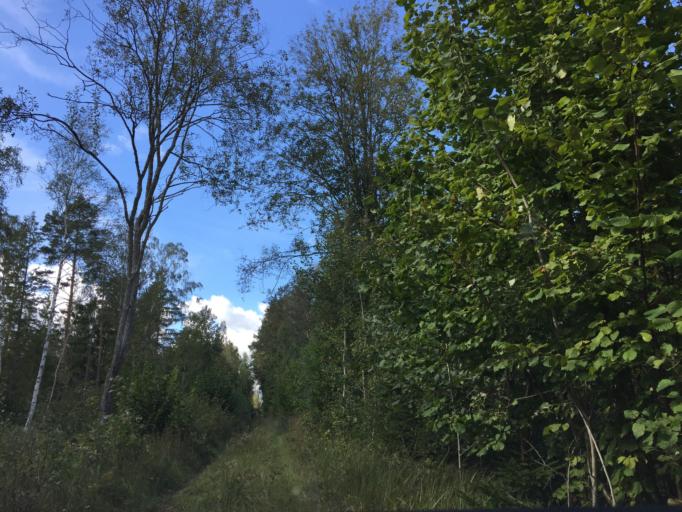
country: LV
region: Kuldigas Rajons
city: Kuldiga
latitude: 56.9796
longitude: 21.8981
